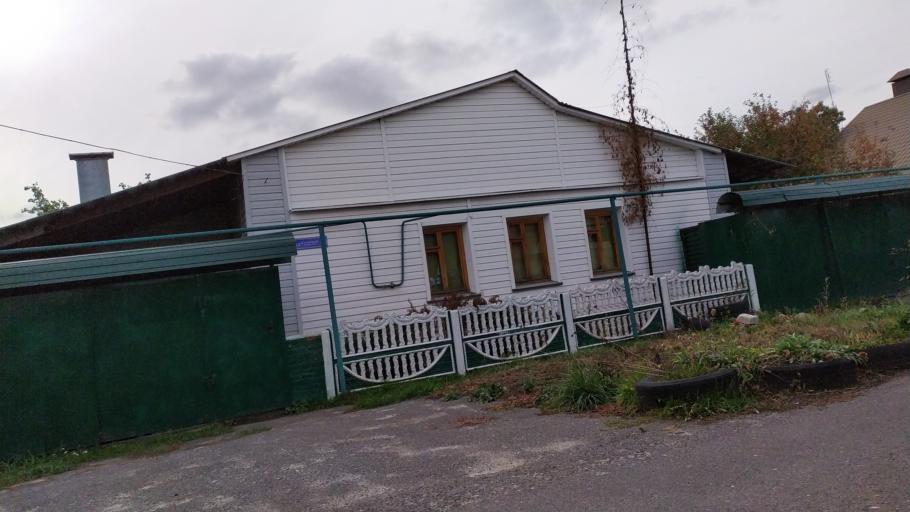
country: RU
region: Kursk
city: Kursk
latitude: 51.6464
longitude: 36.1506
